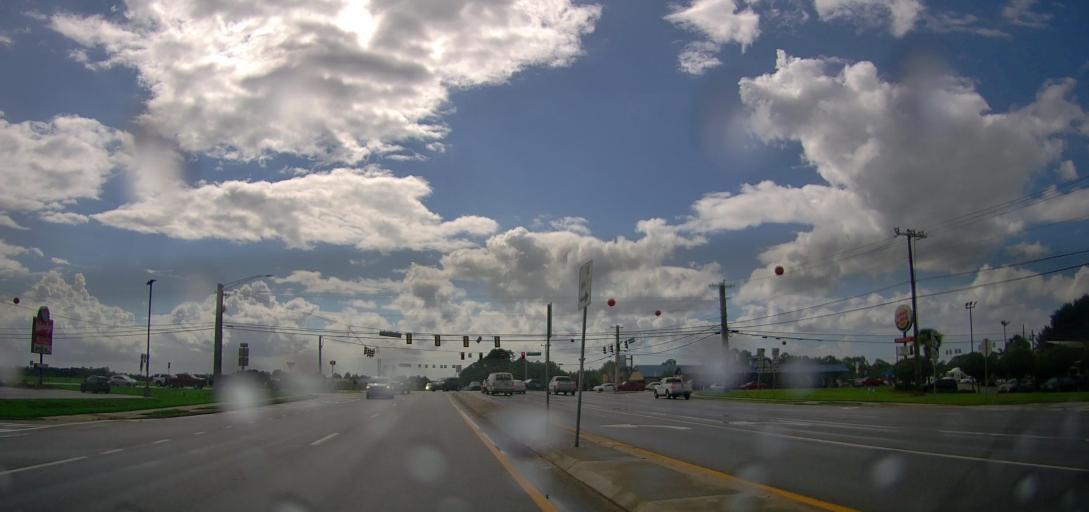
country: US
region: Georgia
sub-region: Coffee County
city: Douglas
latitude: 31.4877
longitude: -82.8502
